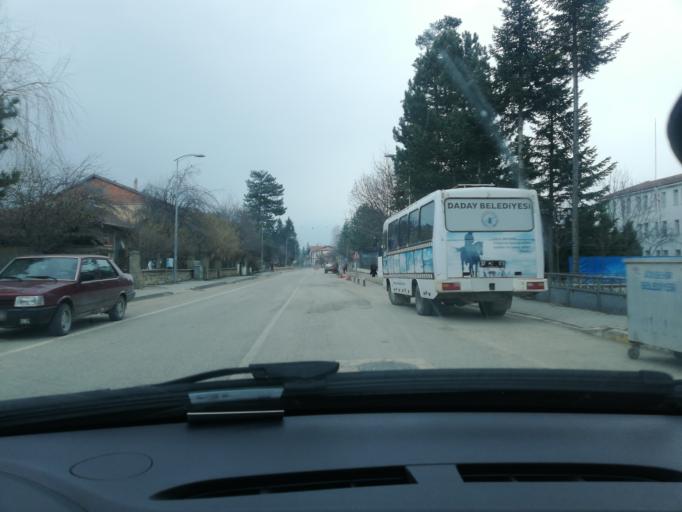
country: TR
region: Kastamonu
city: Daday
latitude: 41.4770
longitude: 33.4652
